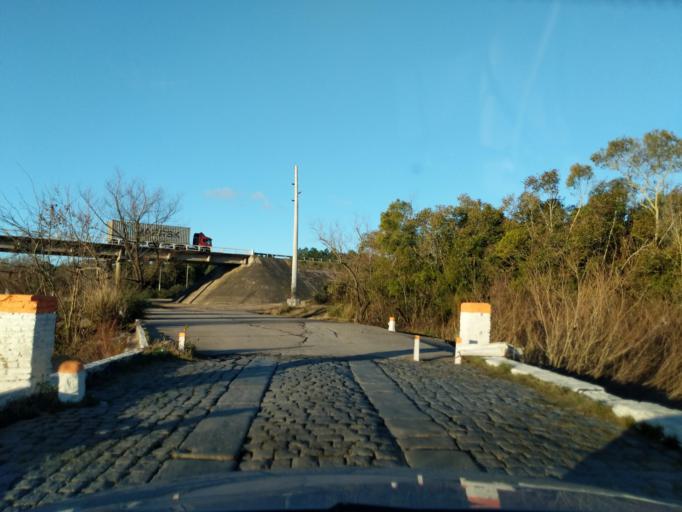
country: UY
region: Florida
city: Florida
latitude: -34.0917
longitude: -56.2041
